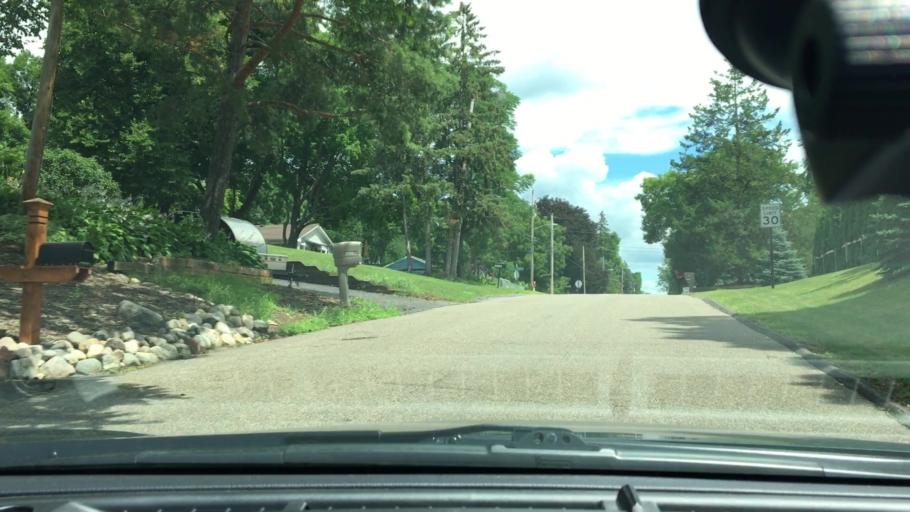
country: US
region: Minnesota
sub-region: Hennepin County
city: New Hope
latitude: 45.0074
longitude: -93.4096
